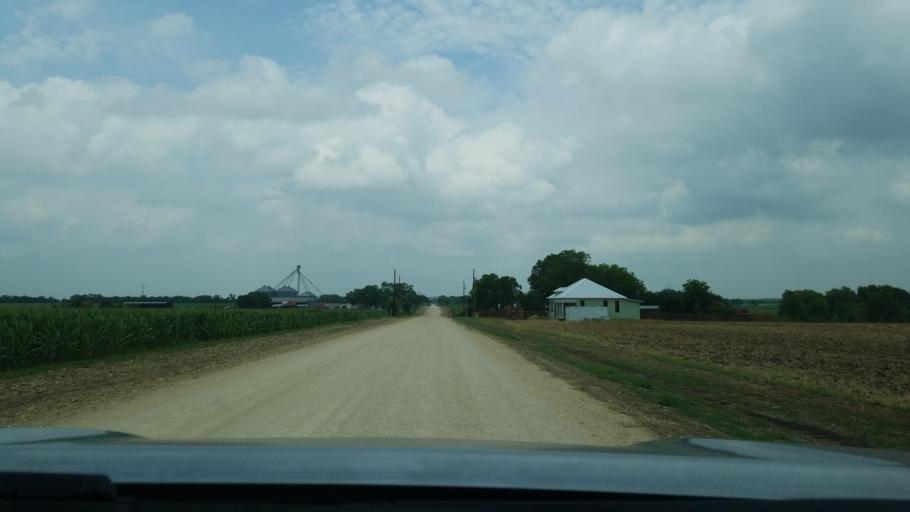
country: US
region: Texas
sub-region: Guadalupe County
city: Geronimo
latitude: 29.6833
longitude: -98.0031
